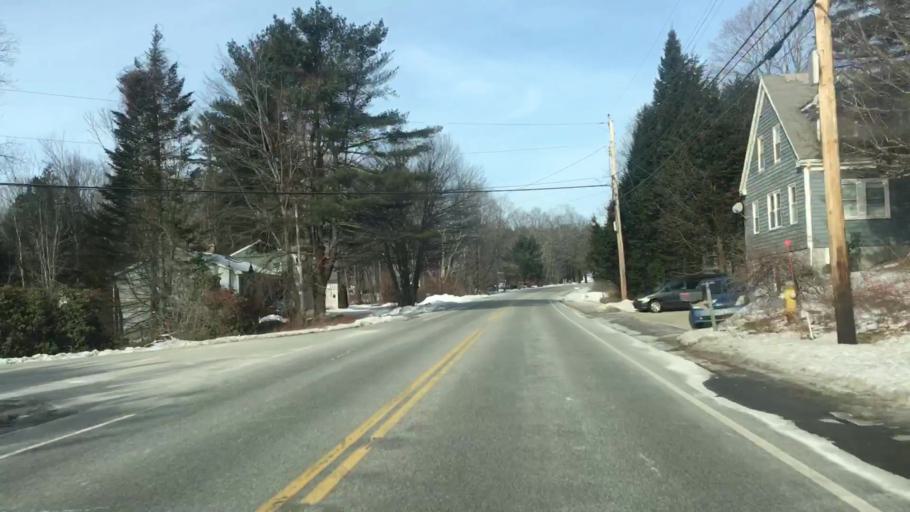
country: US
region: Maine
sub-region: Cumberland County
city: South Windham
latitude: 43.7559
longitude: -70.4250
